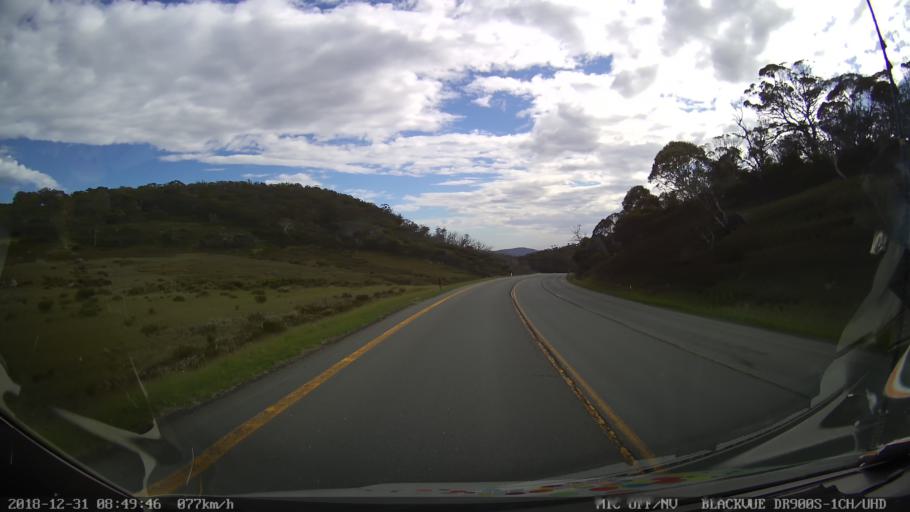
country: AU
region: New South Wales
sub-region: Snowy River
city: Jindabyne
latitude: -36.3588
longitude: 148.5103
